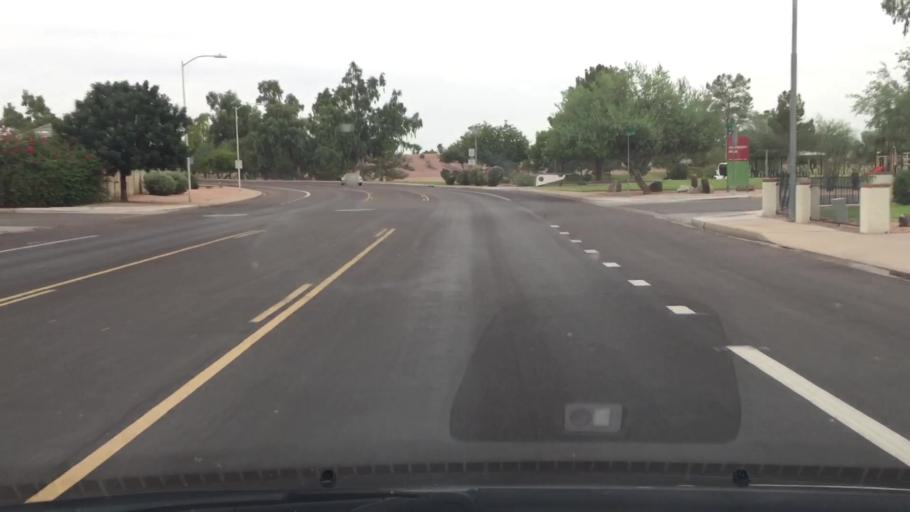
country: US
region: Arizona
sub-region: Maricopa County
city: Gilbert
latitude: 33.3896
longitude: -111.7620
